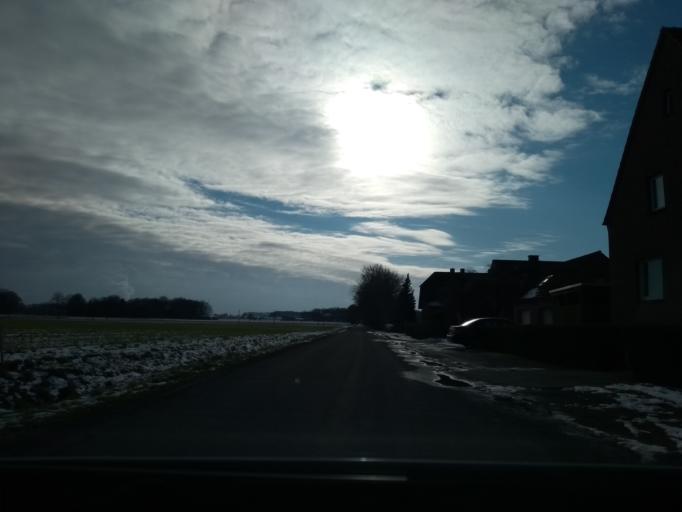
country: DE
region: North Rhine-Westphalia
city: Selm
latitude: 51.6918
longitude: 7.4465
